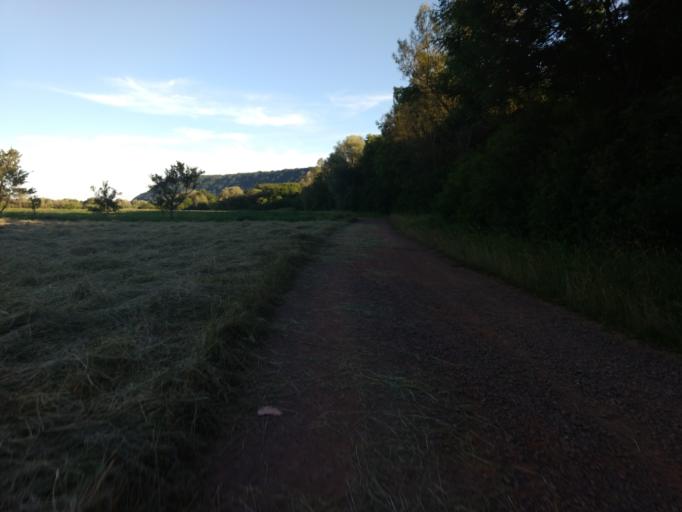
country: DE
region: Saarland
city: Rehlingen-Siersburg
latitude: 49.3631
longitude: 6.6993
